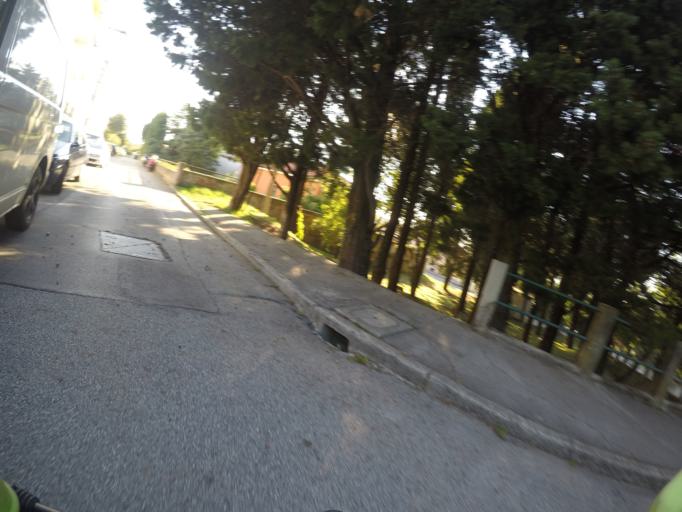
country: IT
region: Friuli Venezia Giulia
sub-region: Provincia di Trieste
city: Trieste
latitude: 45.6498
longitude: 13.7967
